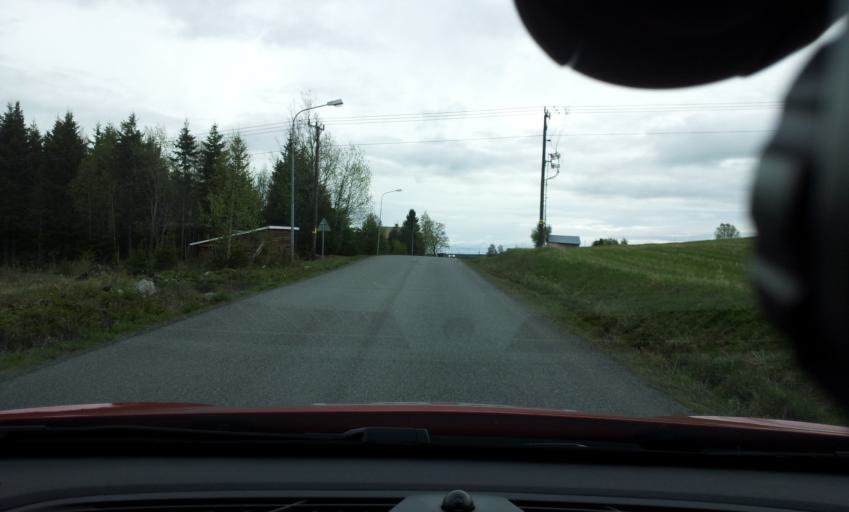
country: SE
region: Jaemtland
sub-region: OEstersunds Kommun
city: Brunflo
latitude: 63.0320
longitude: 14.8118
